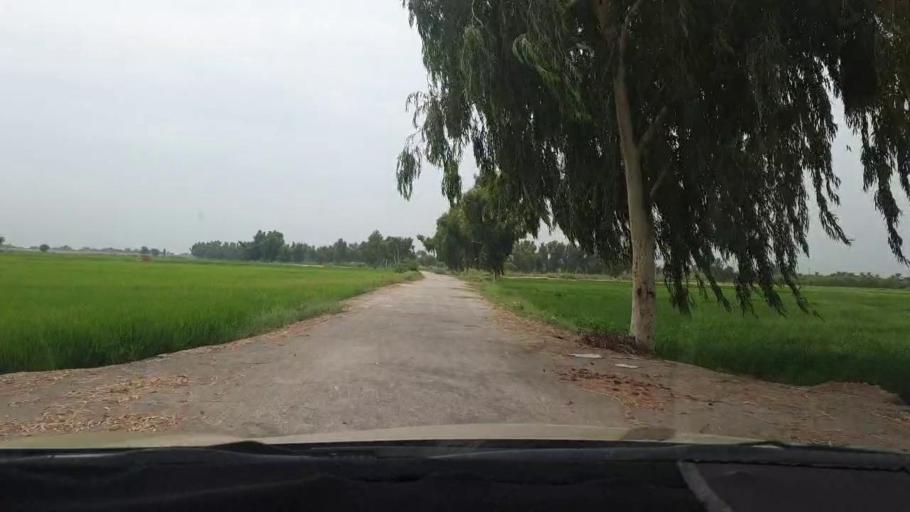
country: PK
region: Sindh
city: Naudero
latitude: 27.6245
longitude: 68.3240
